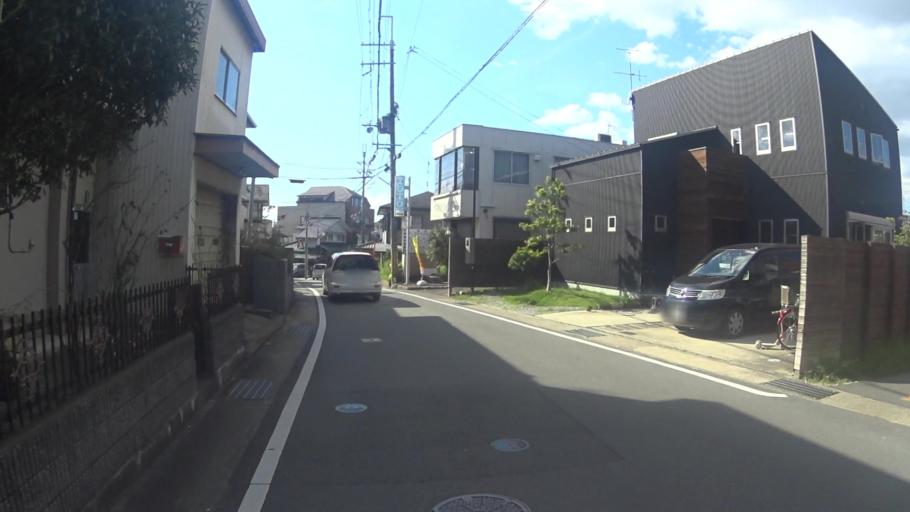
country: JP
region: Kyoto
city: Tanabe
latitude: 34.8400
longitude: 135.7945
